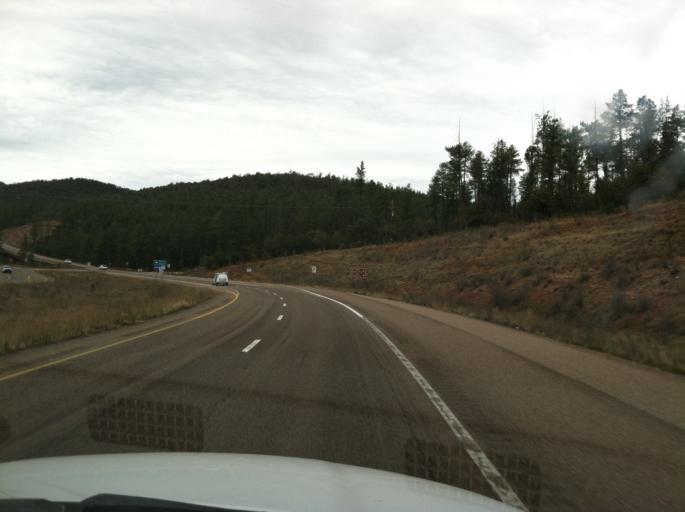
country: US
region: Arizona
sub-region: Gila County
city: Star Valley
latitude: 34.3292
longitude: -111.0898
